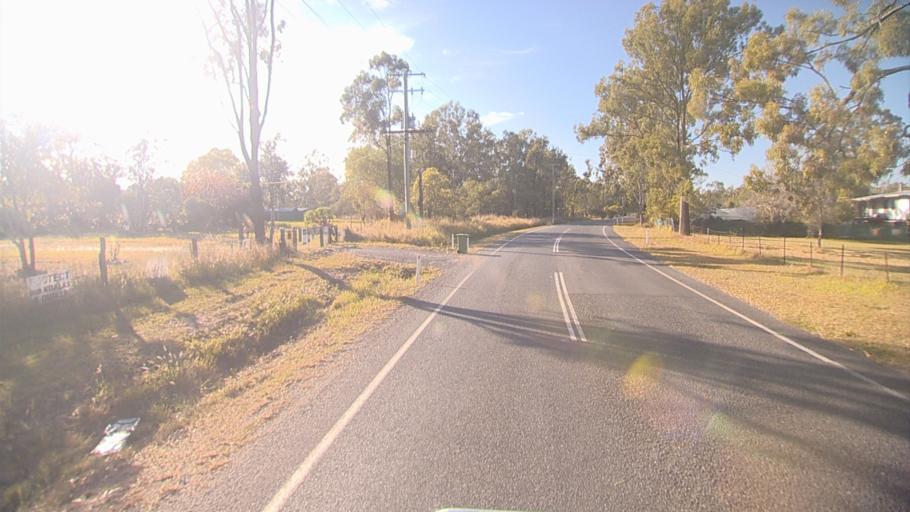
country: AU
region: Queensland
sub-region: Logan
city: North Maclean
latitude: -27.7528
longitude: 152.9993
